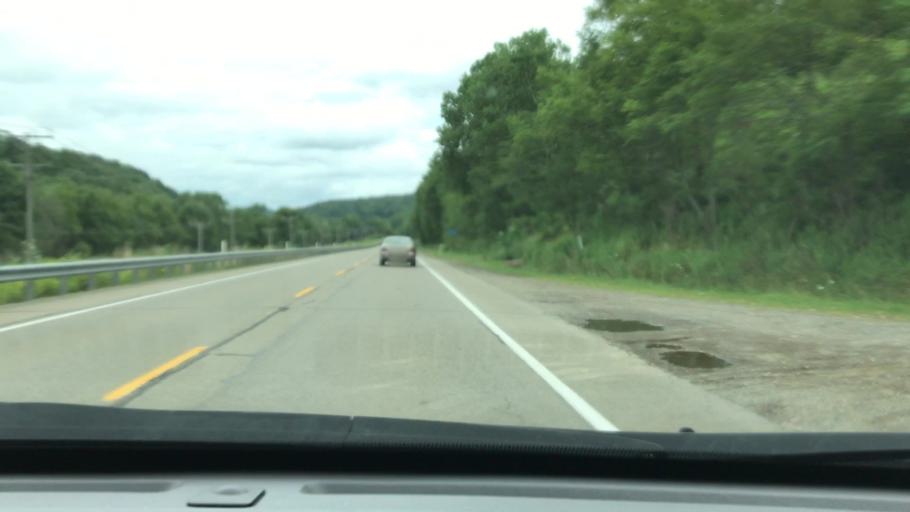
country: US
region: Pennsylvania
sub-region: Elk County
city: Johnsonburg
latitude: 41.5469
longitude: -78.6820
